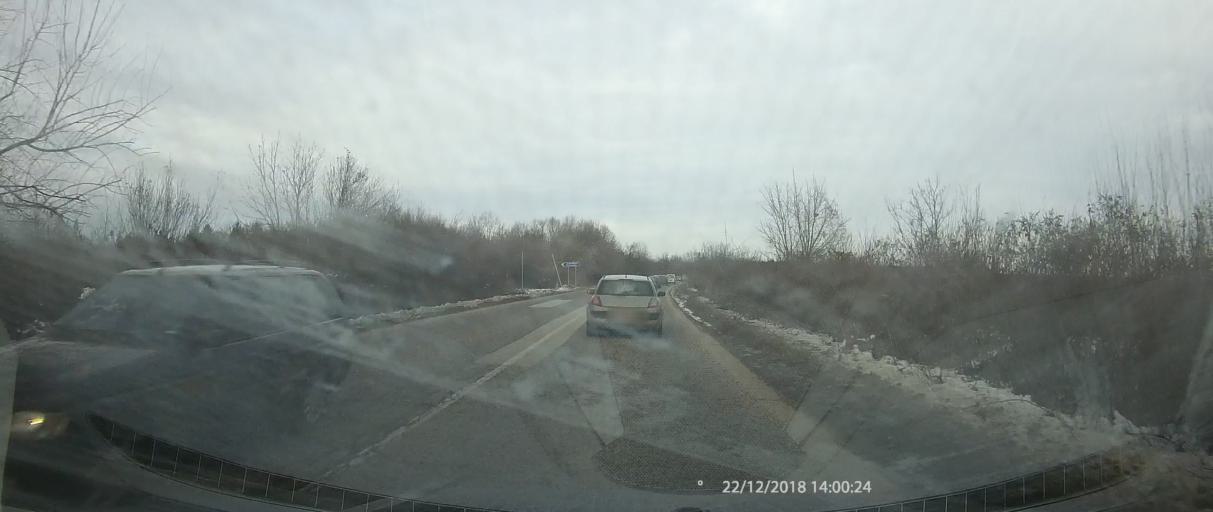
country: BG
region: Pleven
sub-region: Obshtina Dolni Dubnik
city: Dolni Dubnik
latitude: 43.3614
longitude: 24.3436
